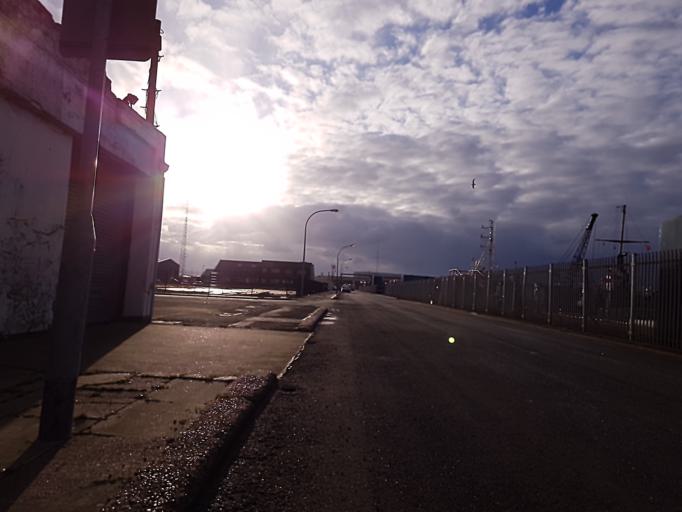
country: GB
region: England
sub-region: North East Lincolnshire
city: Grimsby
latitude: 53.5805
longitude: -0.0604
